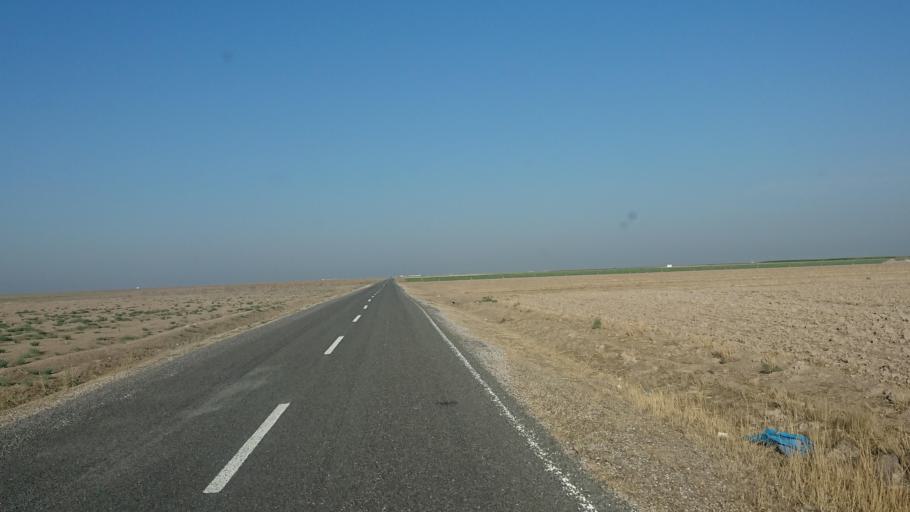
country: TR
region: Aksaray
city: Yesilova
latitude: 38.3877
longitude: 33.7819
